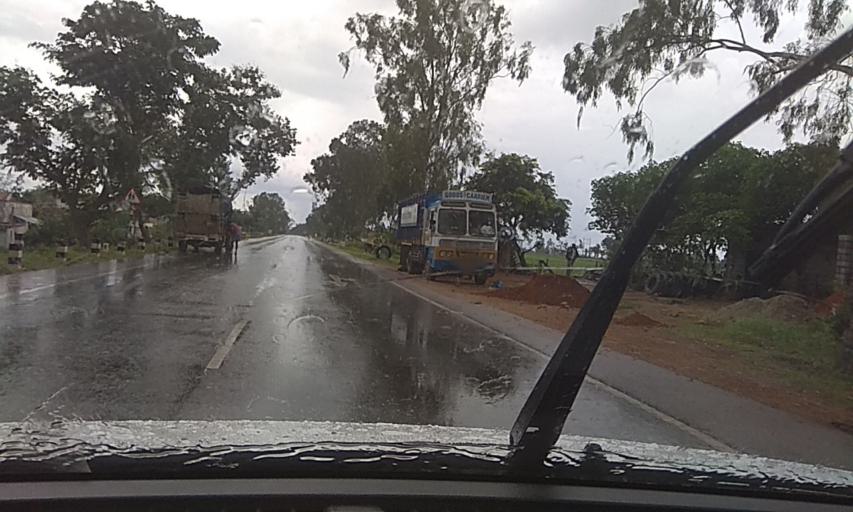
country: IN
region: Karnataka
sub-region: Tumkur
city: Kunigal
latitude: 12.9487
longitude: 77.0273
